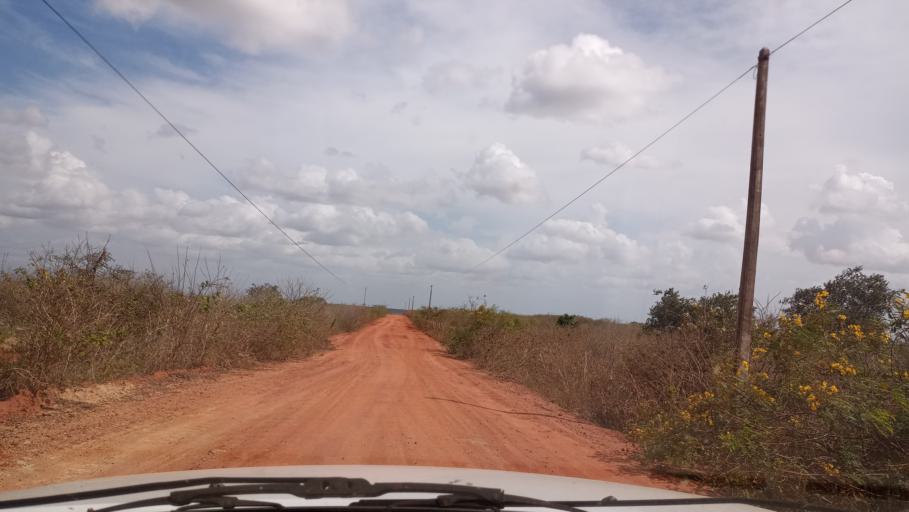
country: BR
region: Rio Grande do Norte
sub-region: Joao Camara
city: Joao Camara
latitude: -5.4533
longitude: -35.8400
